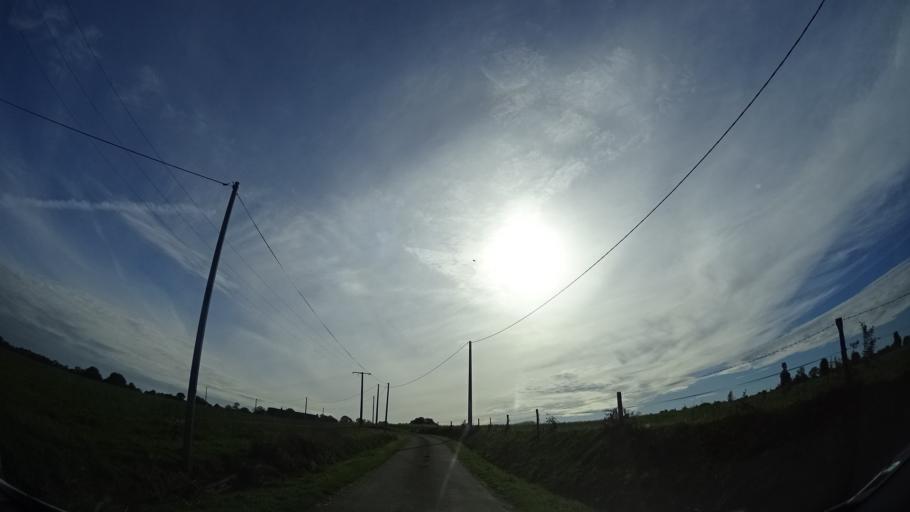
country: FR
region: Brittany
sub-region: Departement d'Ille-et-Vilaine
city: Geveze
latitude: 48.2391
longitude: -1.8291
